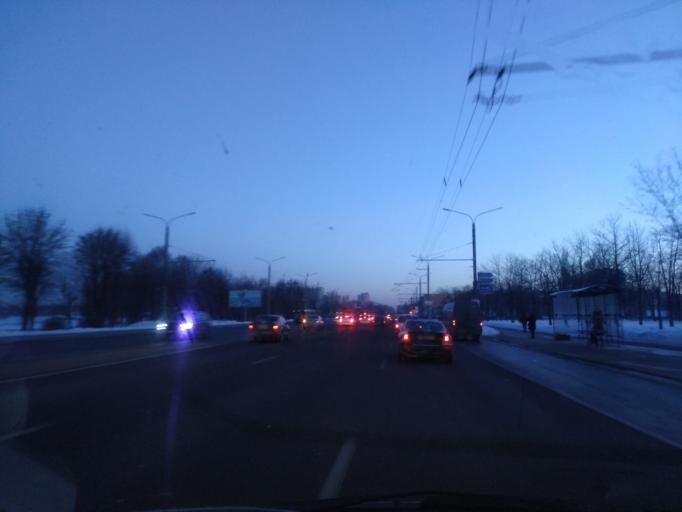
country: BY
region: Mogilev
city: Mahilyow
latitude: 53.8866
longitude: 30.3317
